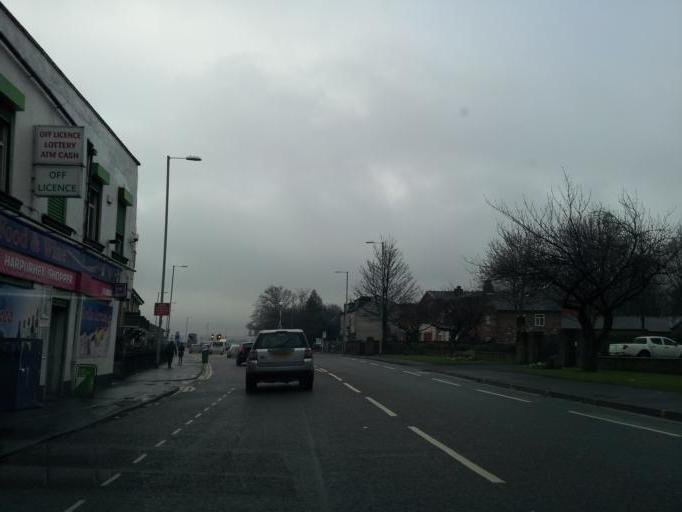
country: GB
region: England
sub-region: Manchester
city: Blackley
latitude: 53.5066
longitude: -2.2177
